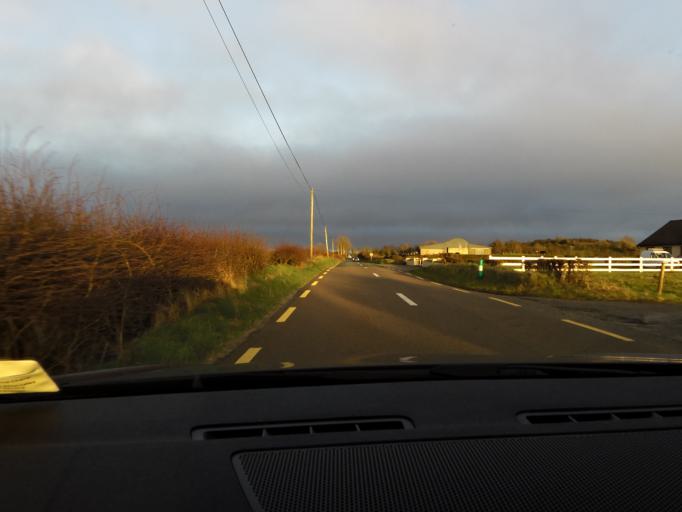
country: IE
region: Connaught
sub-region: Sligo
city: Ballymote
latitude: 54.0329
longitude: -8.5959
